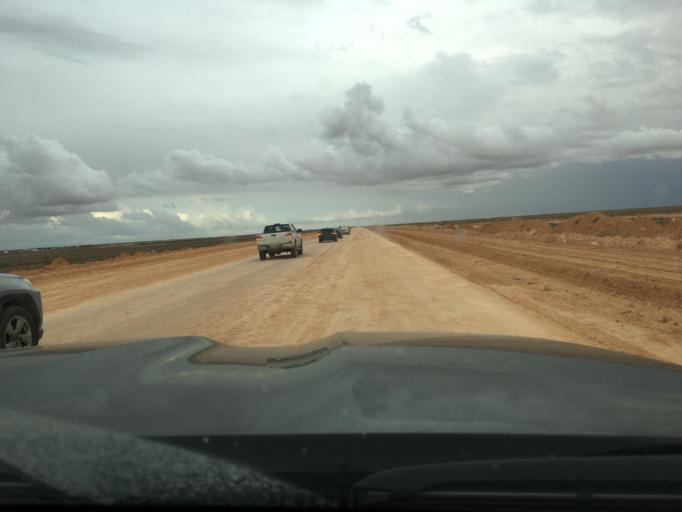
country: TN
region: Madanin
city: Medenine
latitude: 33.2709
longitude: 10.5872
